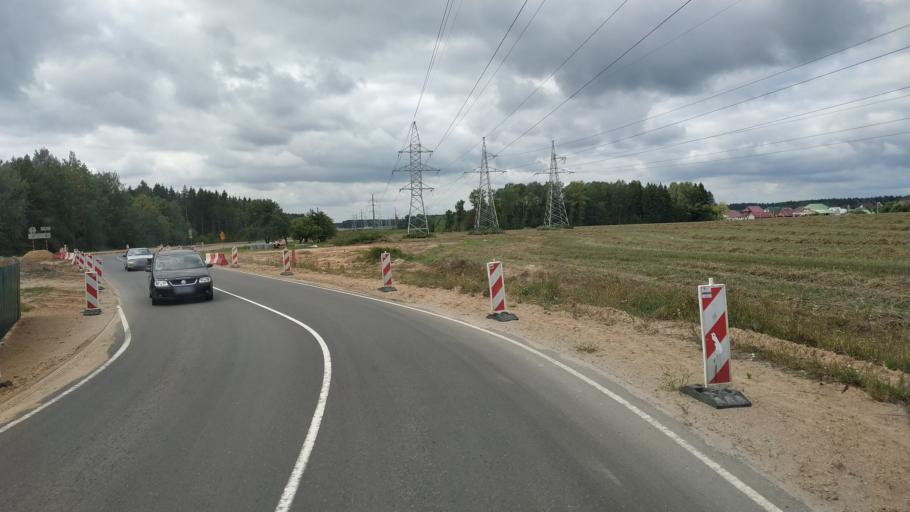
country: BY
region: Mogilev
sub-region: Mahilyowski Rayon
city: Kadino
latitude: 53.8713
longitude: 30.4575
